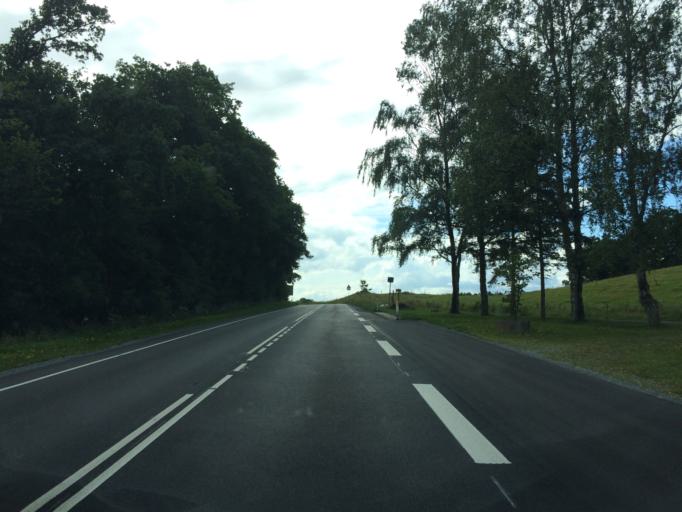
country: DK
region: South Denmark
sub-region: Faaborg-Midtfyn Kommune
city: Faaborg
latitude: 55.1482
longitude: 10.2651
